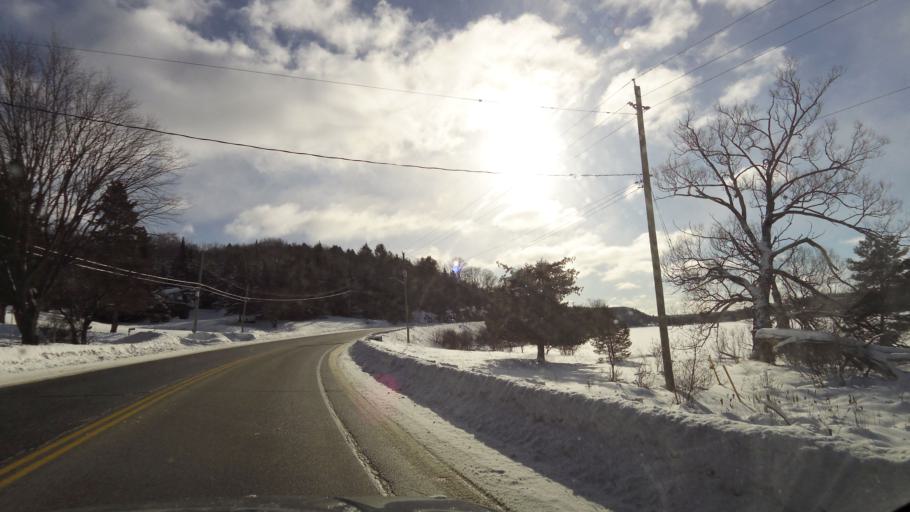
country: CA
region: Ontario
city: Bancroft
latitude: 45.0557
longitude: -78.5141
